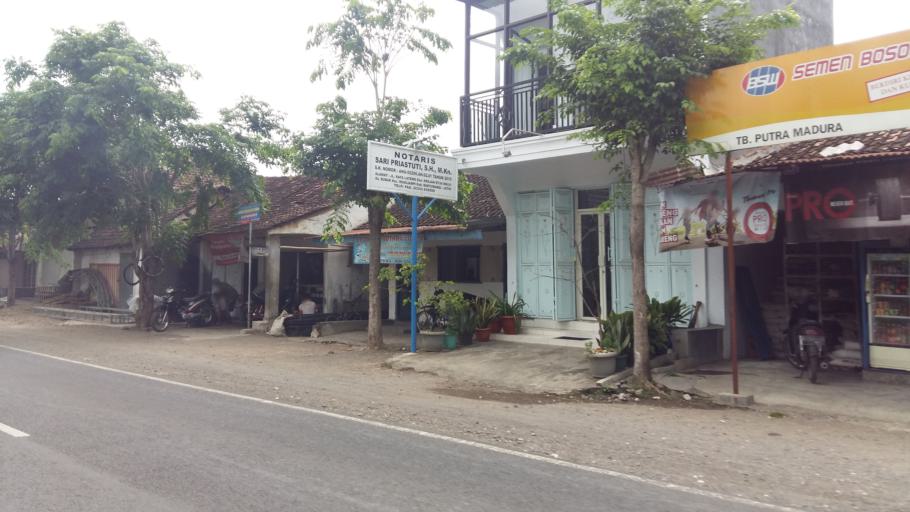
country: ID
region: East Java
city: Krajan
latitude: -8.3275
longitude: 114.2826
